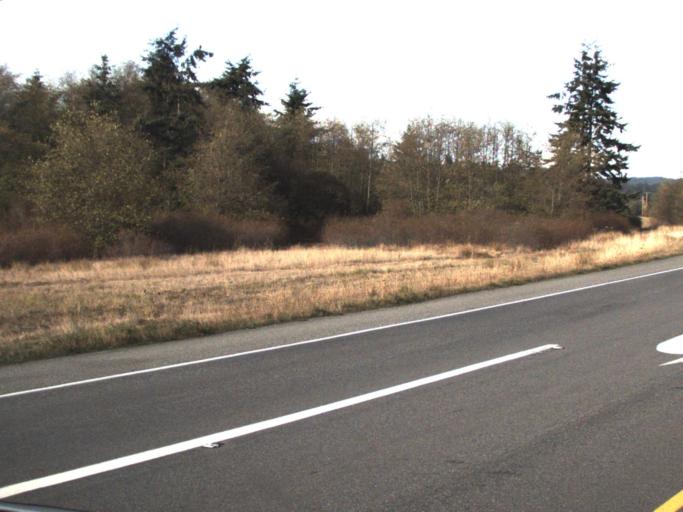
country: US
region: Washington
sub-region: Island County
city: Ault Field
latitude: 48.3770
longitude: -122.6509
